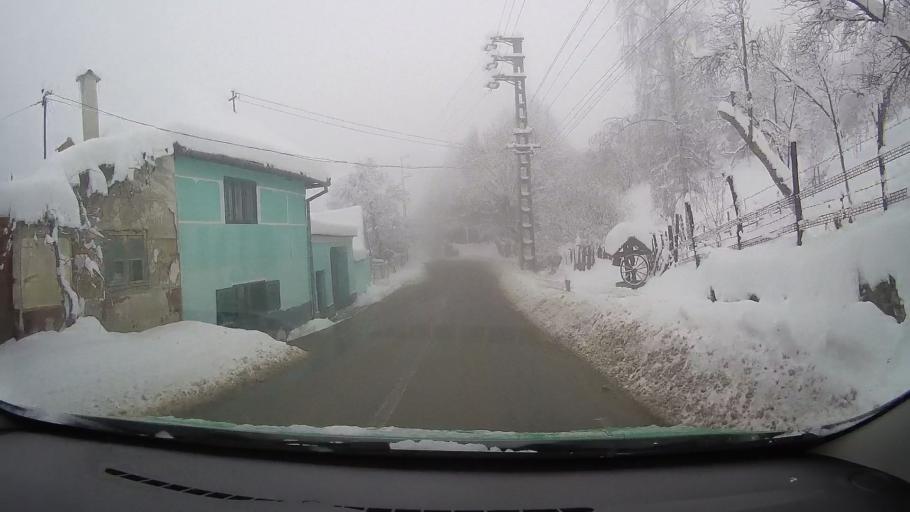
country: RO
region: Sibiu
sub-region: Comuna Poiana Sibiului
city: Poiana Sibiului
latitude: 45.8027
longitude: 23.7760
